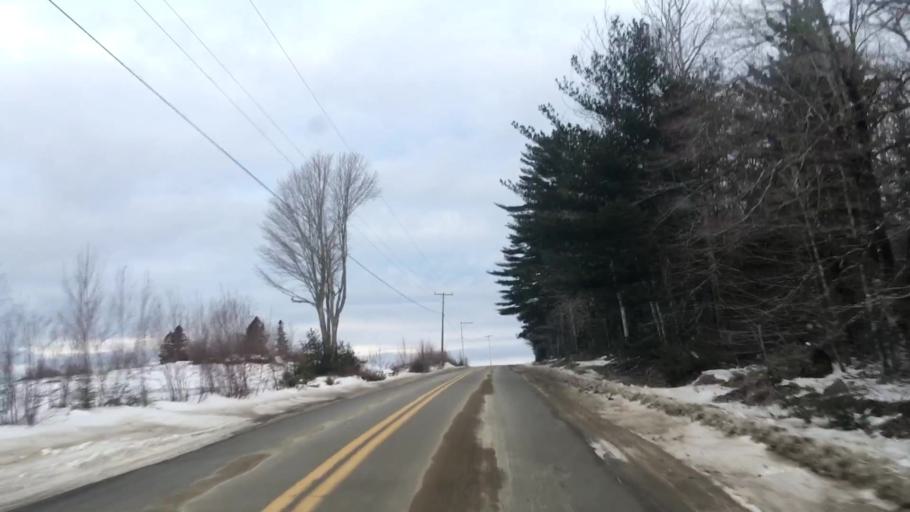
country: US
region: Maine
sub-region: Hancock County
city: Franklin
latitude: 44.8431
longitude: -68.3261
